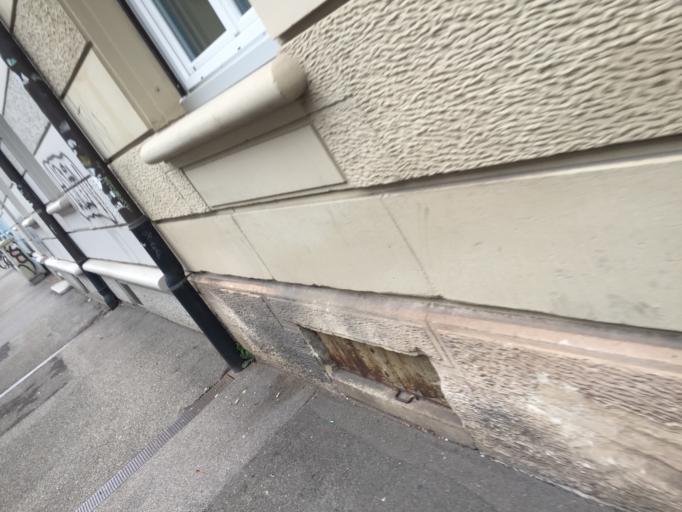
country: CH
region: Basel-City
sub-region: Basel-Stadt
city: Basel
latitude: 47.5441
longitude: 7.5965
